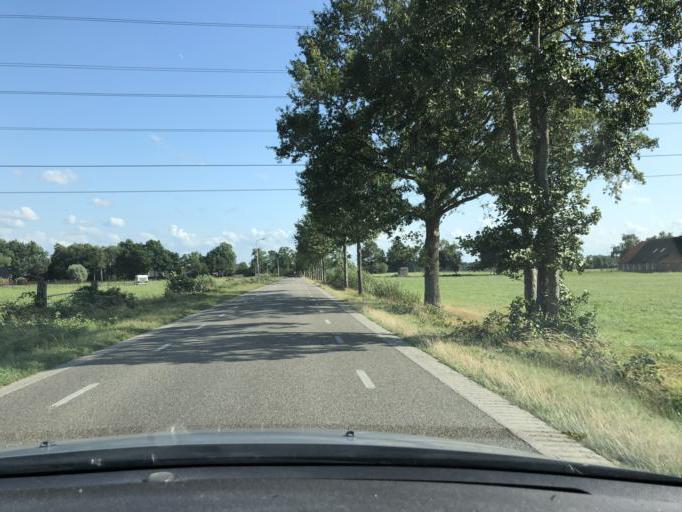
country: NL
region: Overijssel
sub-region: Gemeente Staphorst
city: Staphorst
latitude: 52.6050
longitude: 6.2792
